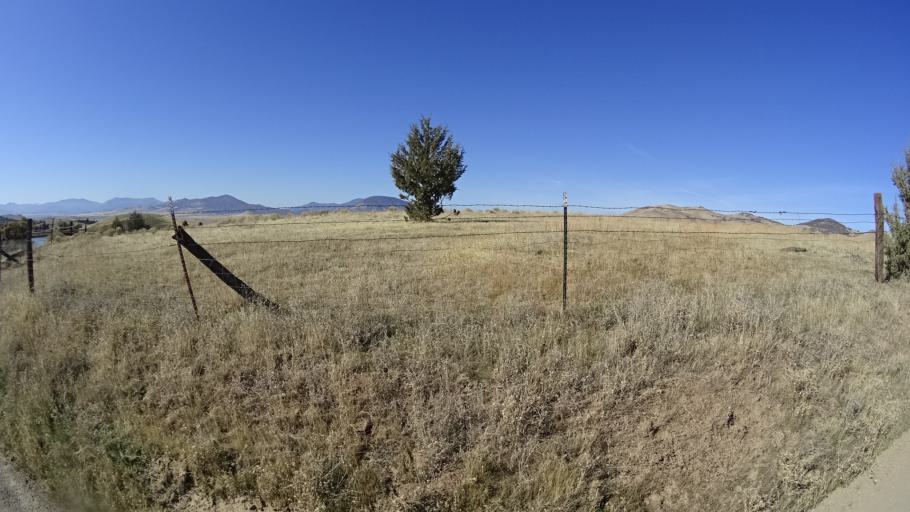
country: US
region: California
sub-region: Siskiyou County
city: Montague
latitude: 41.8157
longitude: -122.3622
